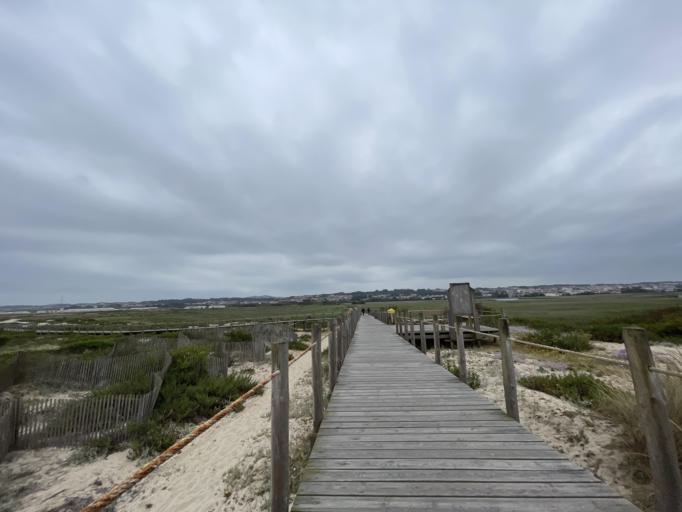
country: PT
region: Aveiro
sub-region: Ovar
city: Esmoriz
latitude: 40.9680
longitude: -8.6502
